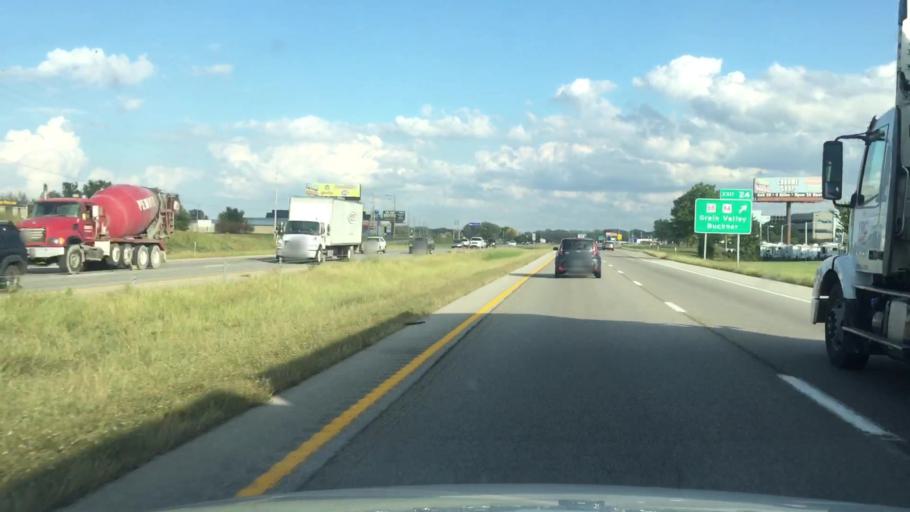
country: US
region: Missouri
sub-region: Jackson County
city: Grain Valley
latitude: 39.0222
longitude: -94.2053
